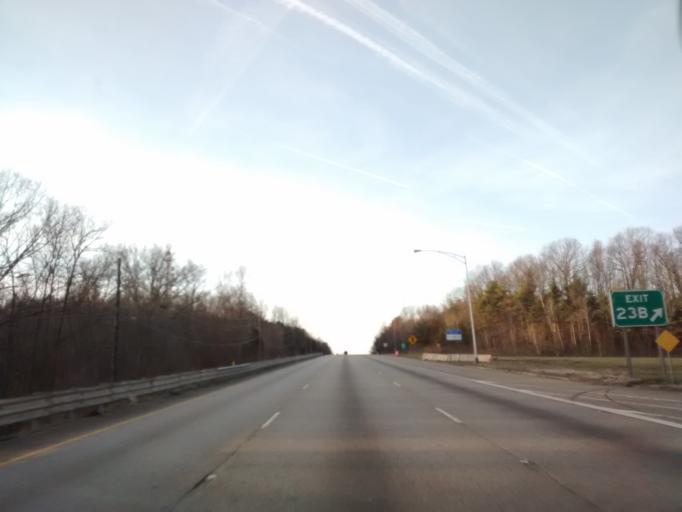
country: US
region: Massachusetts
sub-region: Worcester County
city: Southborough
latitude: 42.2901
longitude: -71.5662
